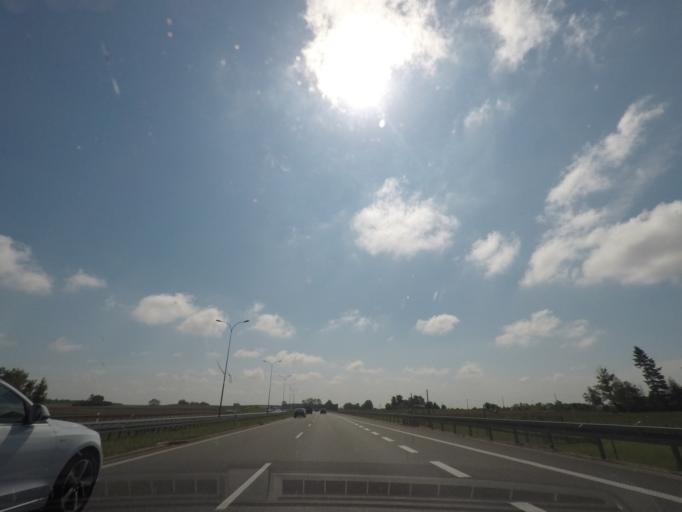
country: PL
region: Kujawsko-Pomorskie
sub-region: Powiat wloclawski
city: Lubien Kujawski
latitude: 52.4626
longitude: 19.1955
